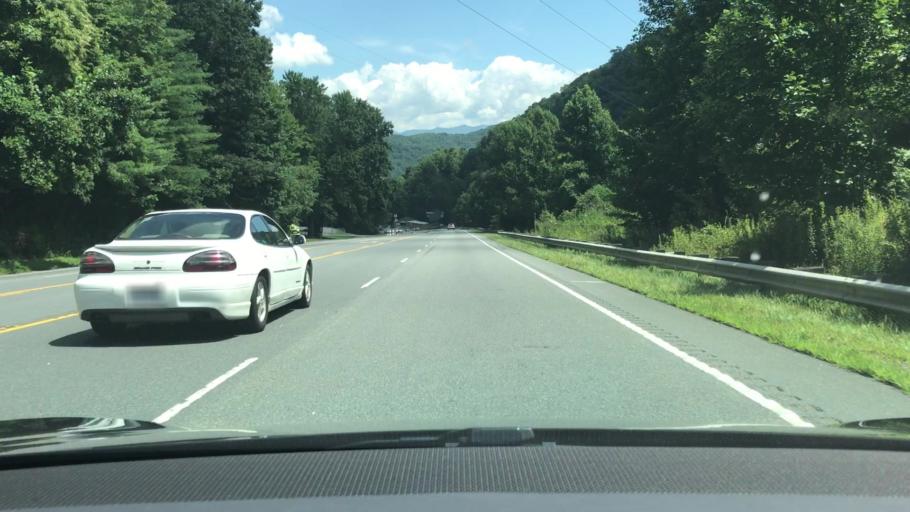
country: US
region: North Carolina
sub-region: Jackson County
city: Sylva
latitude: 35.2728
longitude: -83.2912
